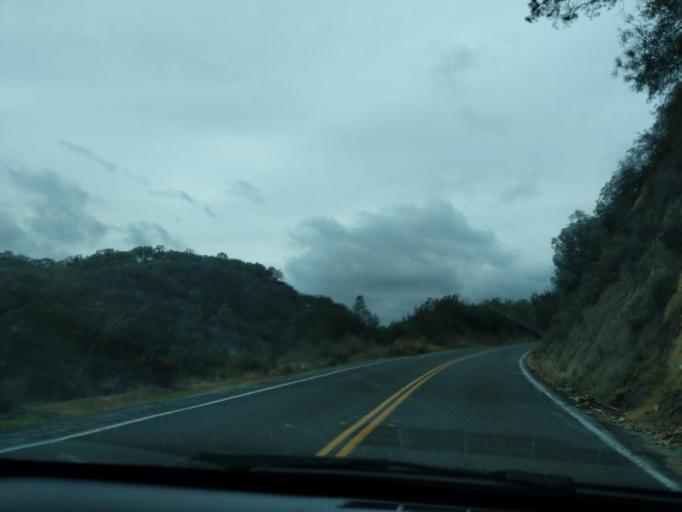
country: US
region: California
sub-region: Monterey County
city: Soledad
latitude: 36.5876
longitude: -121.1958
